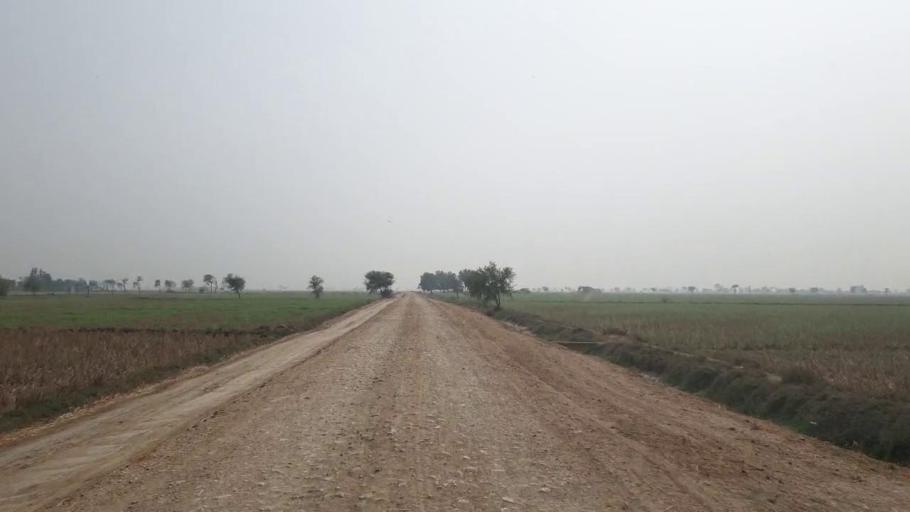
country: PK
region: Sindh
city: Kario
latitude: 24.6443
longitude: 68.5954
